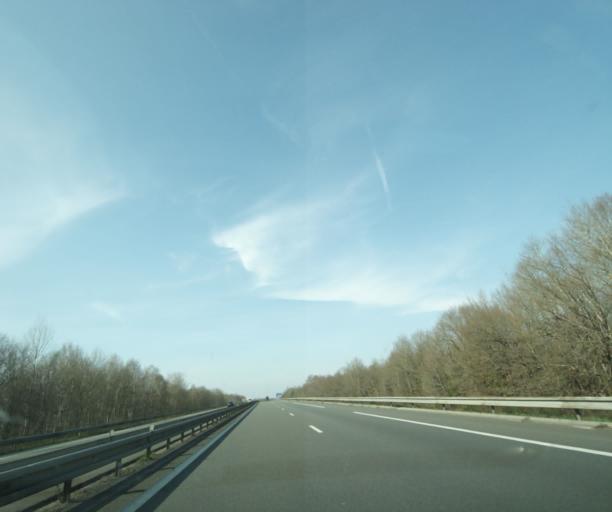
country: FR
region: Centre
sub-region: Departement du Loir-et-Cher
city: Salbris
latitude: 47.4328
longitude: 2.0137
